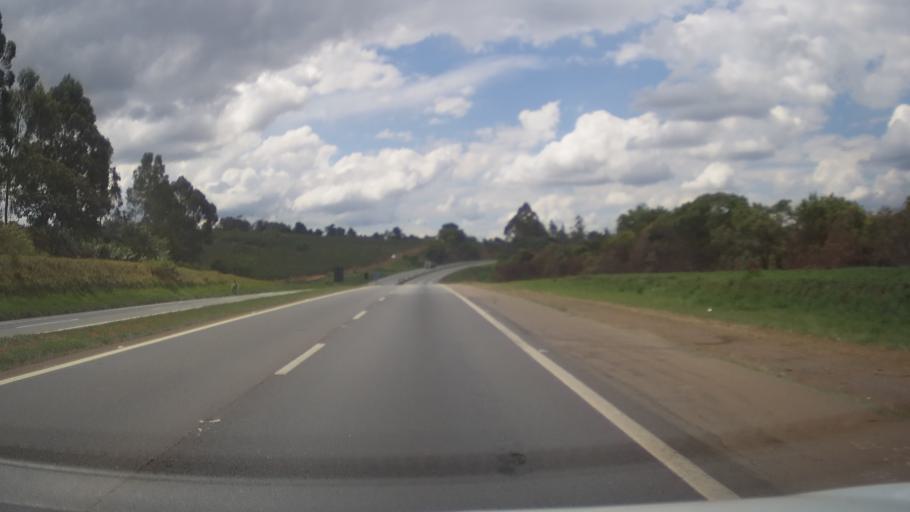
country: BR
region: Minas Gerais
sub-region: Nepomuceno
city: Nepomuceno
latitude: -21.2510
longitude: -45.1384
